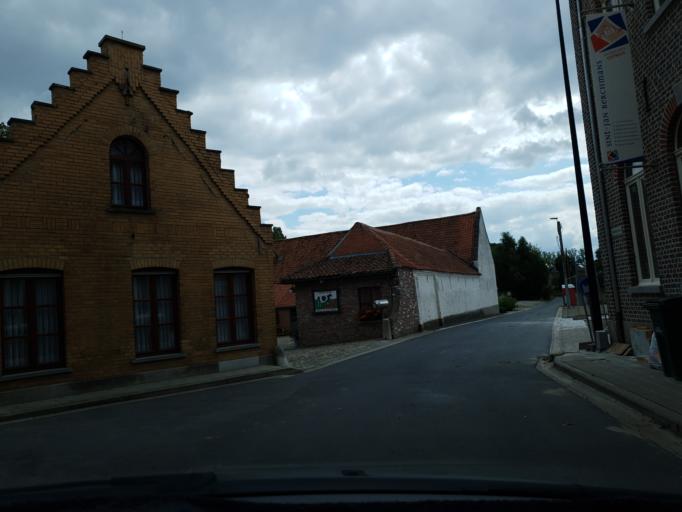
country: BE
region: Flanders
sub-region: Provincie West-Vlaanderen
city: Avelgem
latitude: 50.7550
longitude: 3.4297
